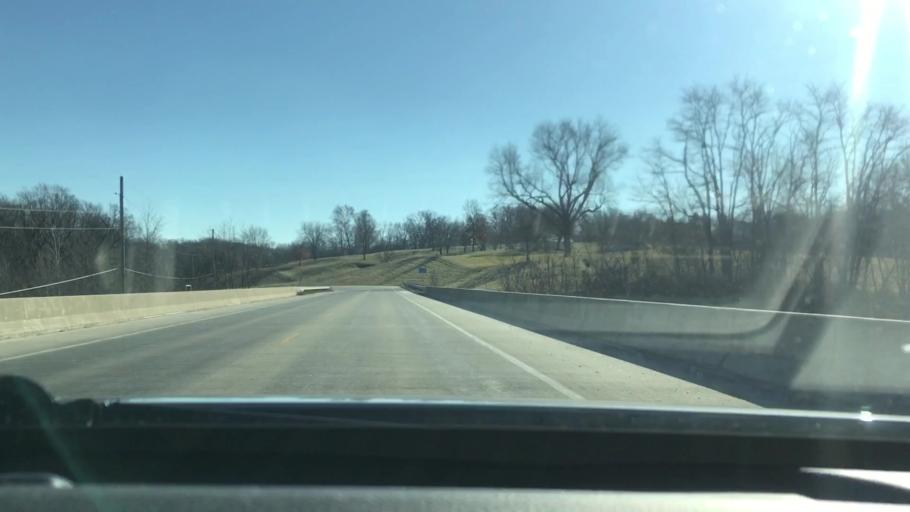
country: US
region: Missouri
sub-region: Platte County
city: Platte City
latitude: 39.3692
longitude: -94.7867
